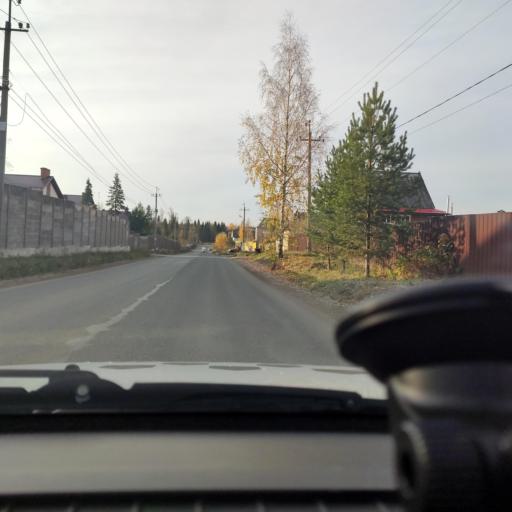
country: RU
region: Perm
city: Ferma
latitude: 57.9434
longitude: 56.4227
